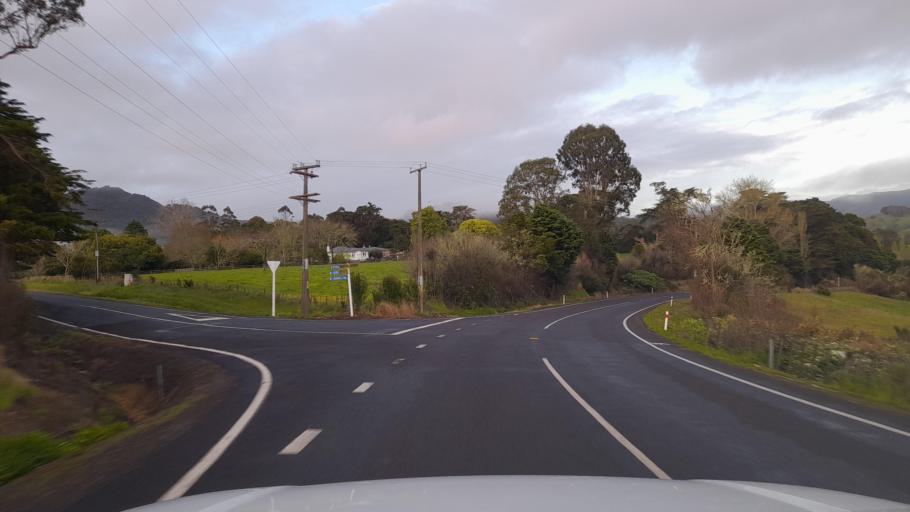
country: NZ
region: Northland
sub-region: Kaipara District
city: Dargaville
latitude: -35.7143
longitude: 173.9540
